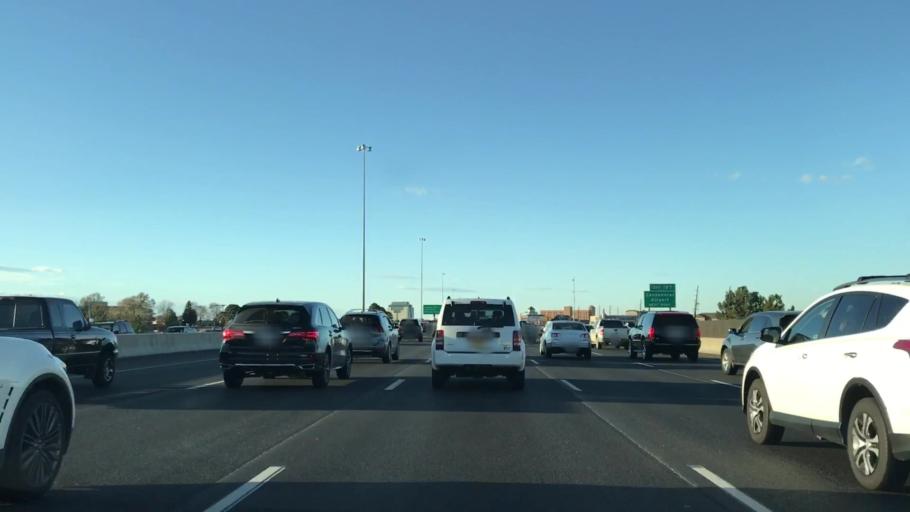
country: US
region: Colorado
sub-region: Arapahoe County
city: Centennial
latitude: 39.5802
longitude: -104.8759
